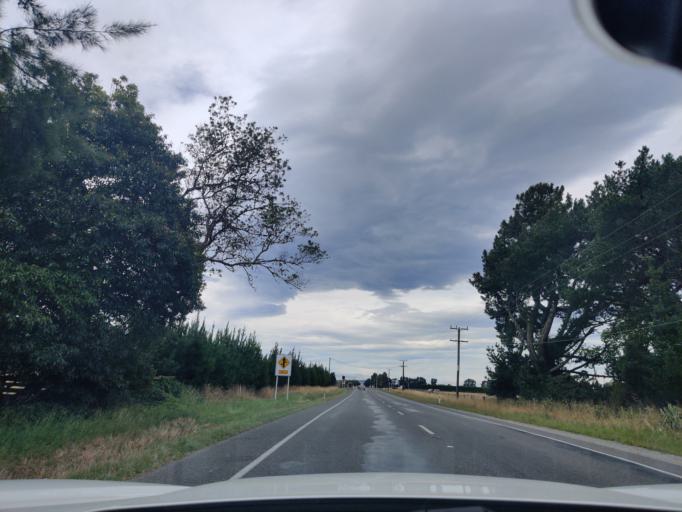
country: NZ
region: Wellington
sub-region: Masterton District
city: Masterton
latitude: -40.9833
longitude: 175.5818
